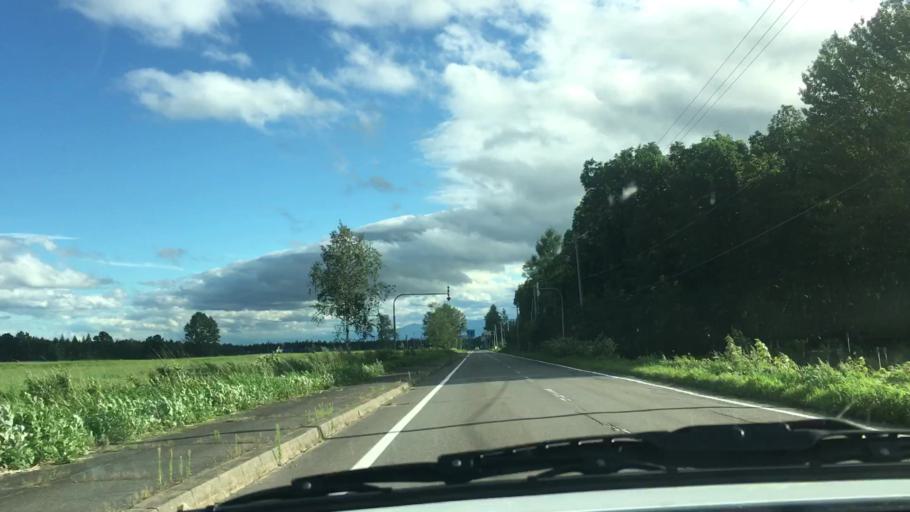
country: JP
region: Hokkaido
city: Otofuke
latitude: 43.1729
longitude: 143.0060
